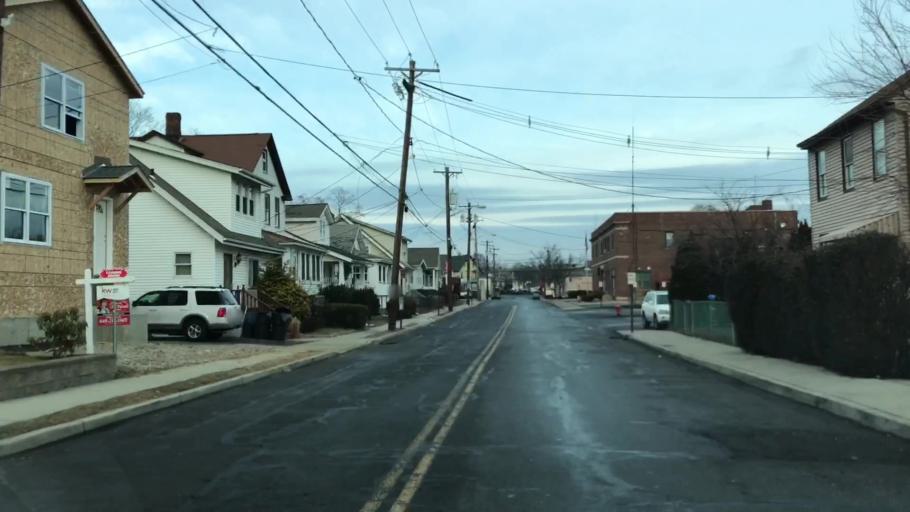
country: US
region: New York
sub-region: Rockland County
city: Haverstraw
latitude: 41.1944
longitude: -73.9640
